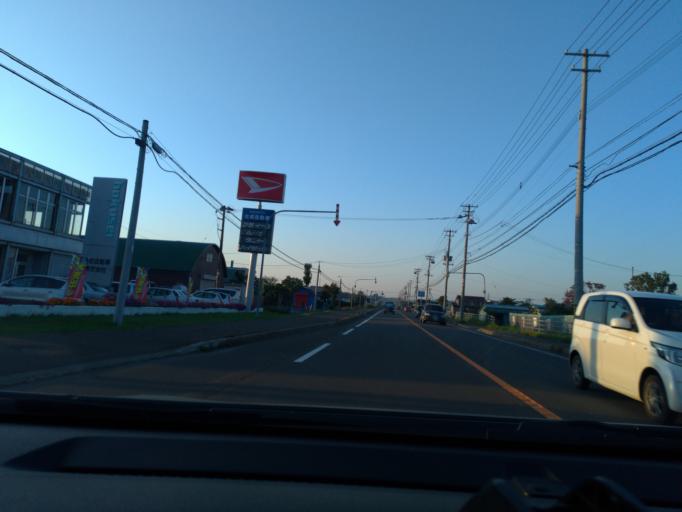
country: JP
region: Hokkaido
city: Tobetsu
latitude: 43.2004
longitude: 141.5218
